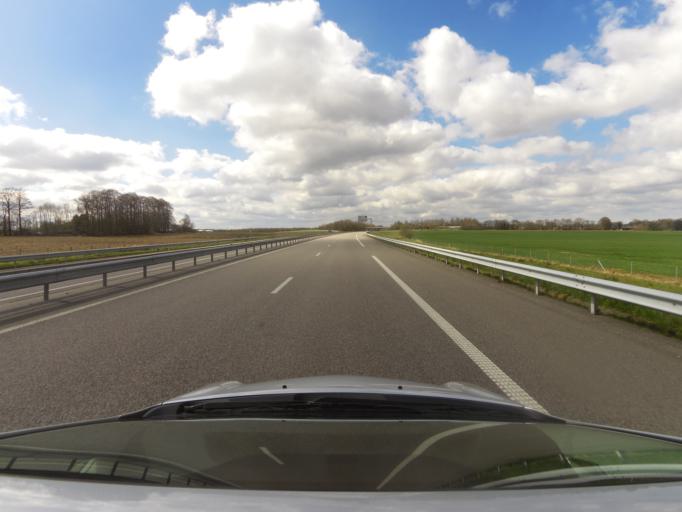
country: FR
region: Haute-Normandie
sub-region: Departement de la Seine-Maritime
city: Yerville
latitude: 49.6528
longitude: 0.8538
